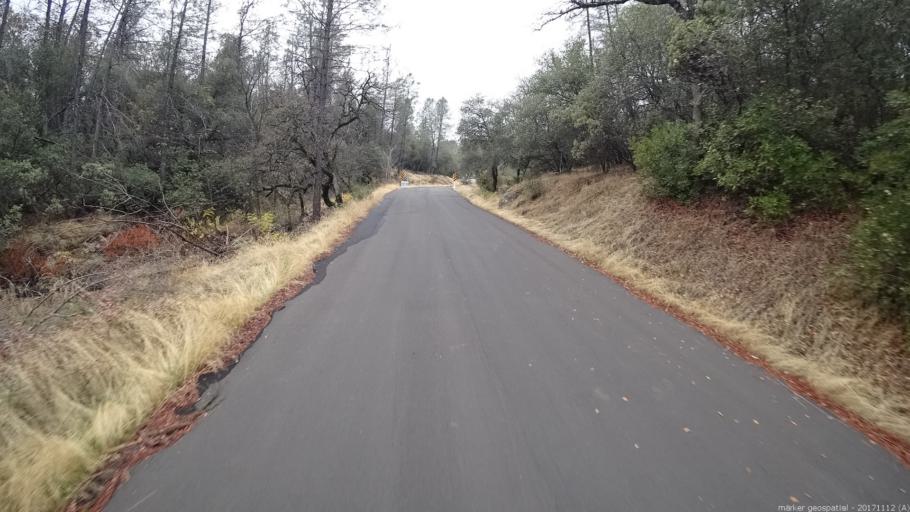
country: US
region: California
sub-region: Shasta County
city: Shasta
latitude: 40.5930
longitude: -122.4822
